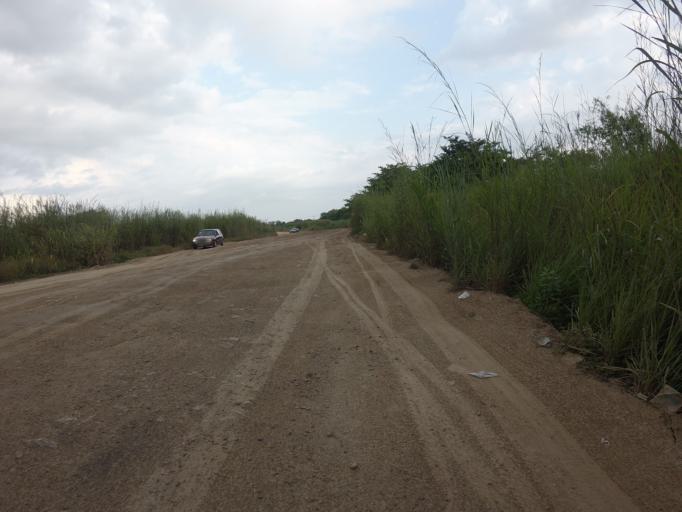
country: GH
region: Volta
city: Ho
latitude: 6.4294
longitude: 0.5085
